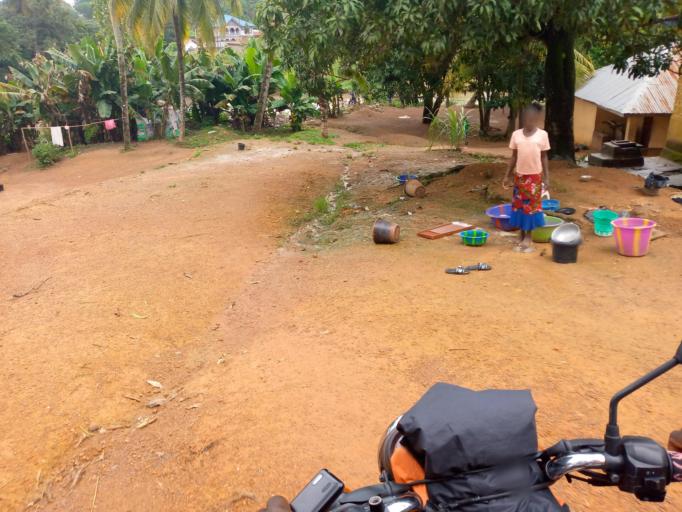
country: SL
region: Eastern Province
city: Kenema
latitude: 7.8720
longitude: -11.1845
